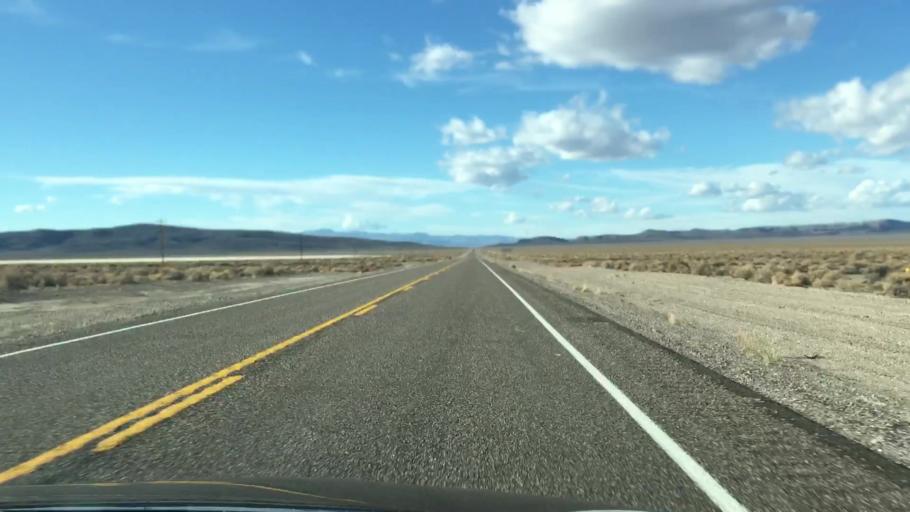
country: US
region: Nevada
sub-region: Nye County
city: Beatty
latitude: 37.1385
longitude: -116.8558
